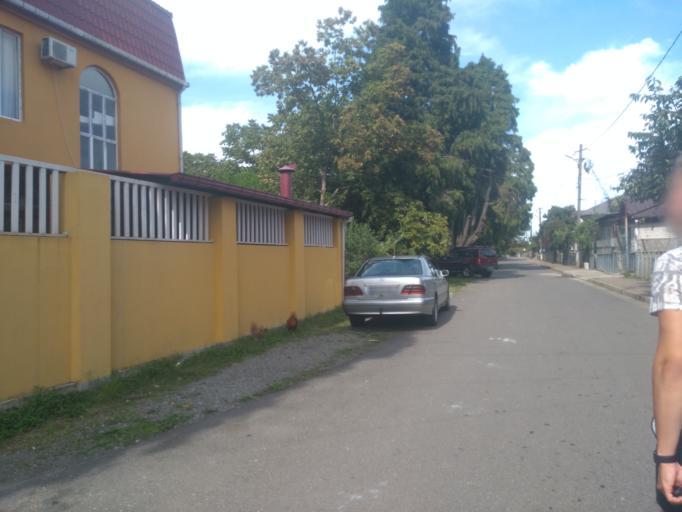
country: GE
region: Ajaria
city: Kobuleti
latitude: 41.8635
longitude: 41.7832
